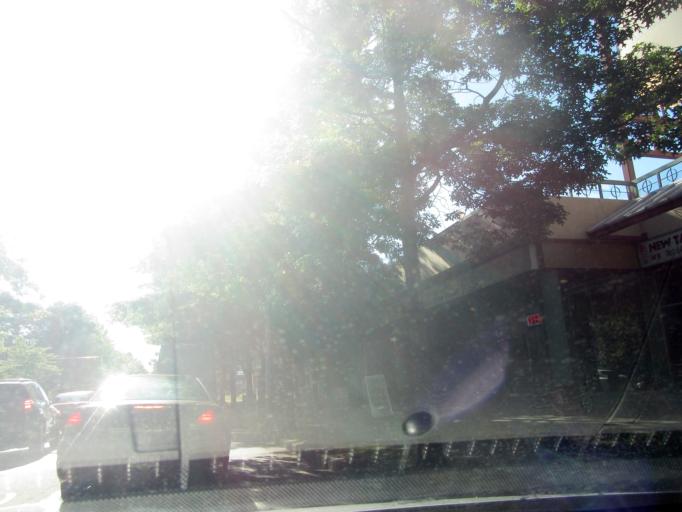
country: CA
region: British Columbia
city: Richmond
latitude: 49.1774
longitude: -123.1273
